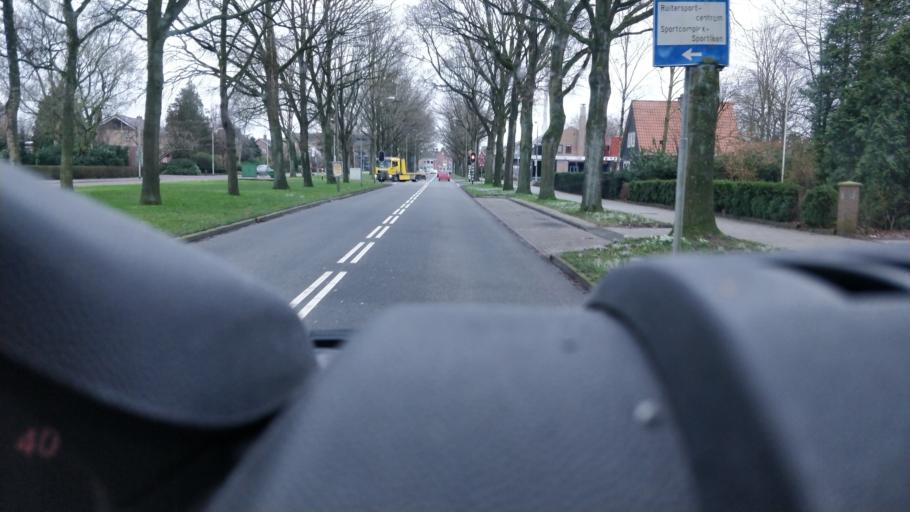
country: NL
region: Flevoland
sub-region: Gemeente Noordoostpolder
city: Emmeloord
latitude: 52.7156
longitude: 5.7538
